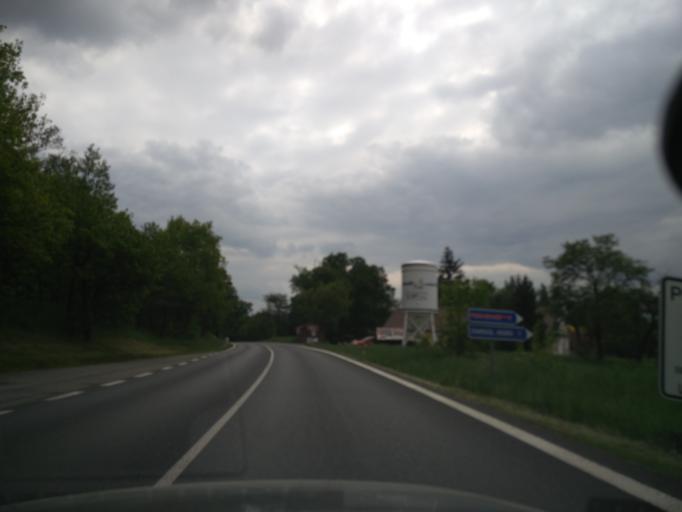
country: CZ
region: Central Bohemia
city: Milin
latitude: 49.5842
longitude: 14.0711
